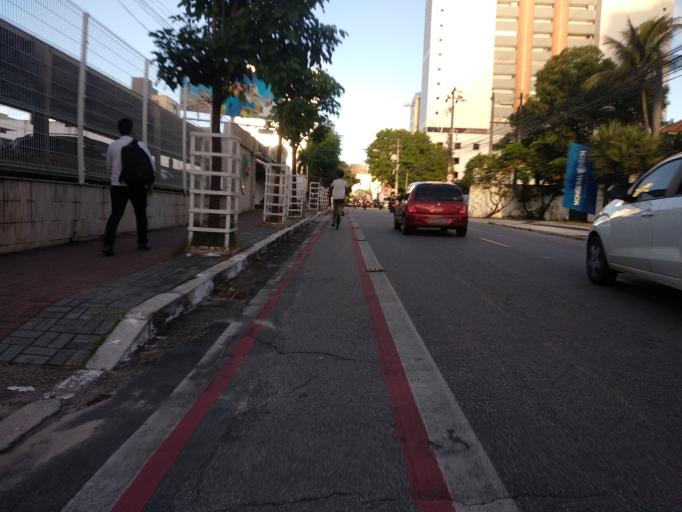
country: BR
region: Ceara
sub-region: Fortaleza
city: Fortaleza
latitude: -3.7309
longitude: -38.5146
